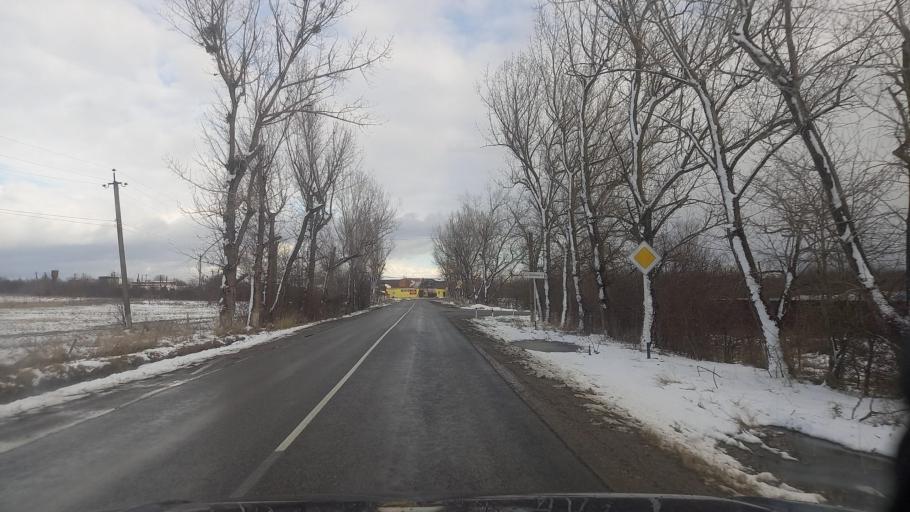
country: RU
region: Krasnodarskiy
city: Smolenskaya
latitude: 44.7759
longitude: 38.8311
